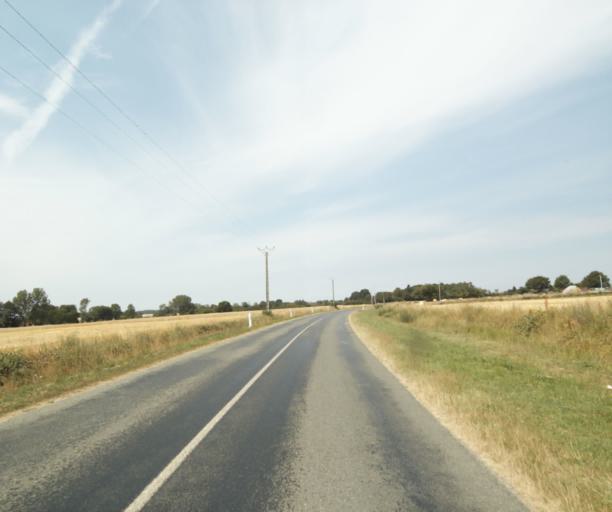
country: FR
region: Centre
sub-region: Departement d'Eure-et-Loir
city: La Bazoche-Gouet
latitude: 48.1747
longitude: 1.0098
